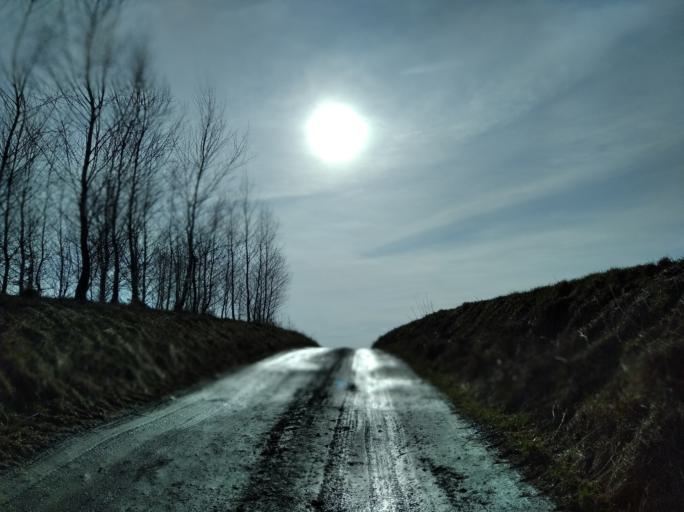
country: PL
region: Subcarpathian Voivodeship
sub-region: Powiat brzozowski
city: Humniska
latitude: 49.6602
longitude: 22.0493
